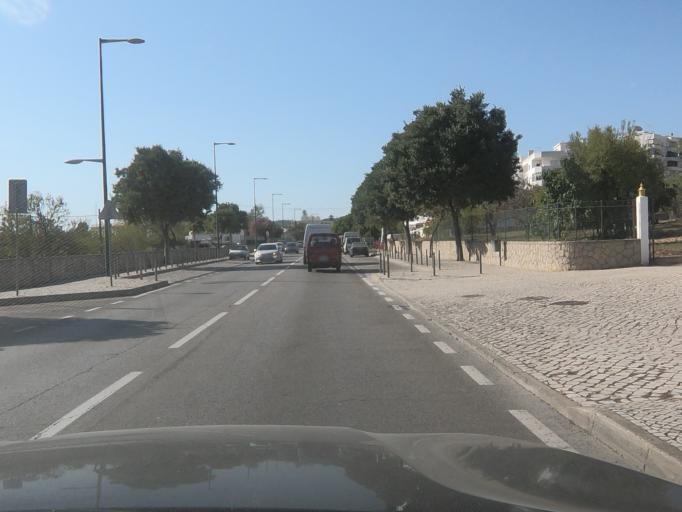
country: PT
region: Faro
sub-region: Loule
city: Loule
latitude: 37.1321
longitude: -8.0189
